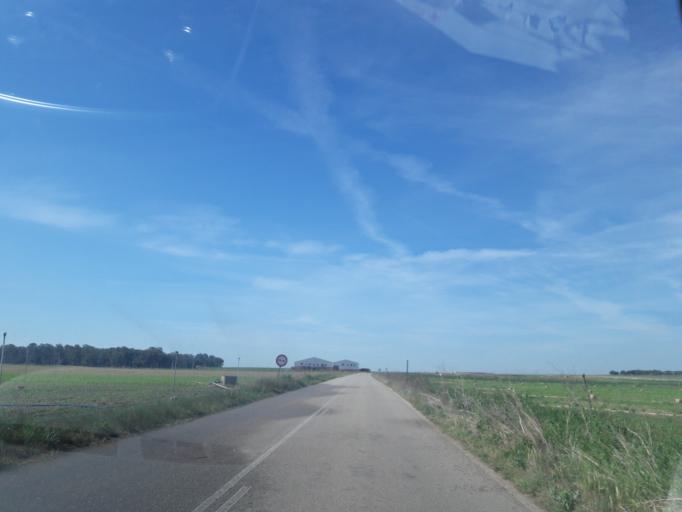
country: ES
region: Castille and Leon
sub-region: Provincia de Salamanca
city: Villoruela
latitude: 41.0396
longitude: -5.3872
